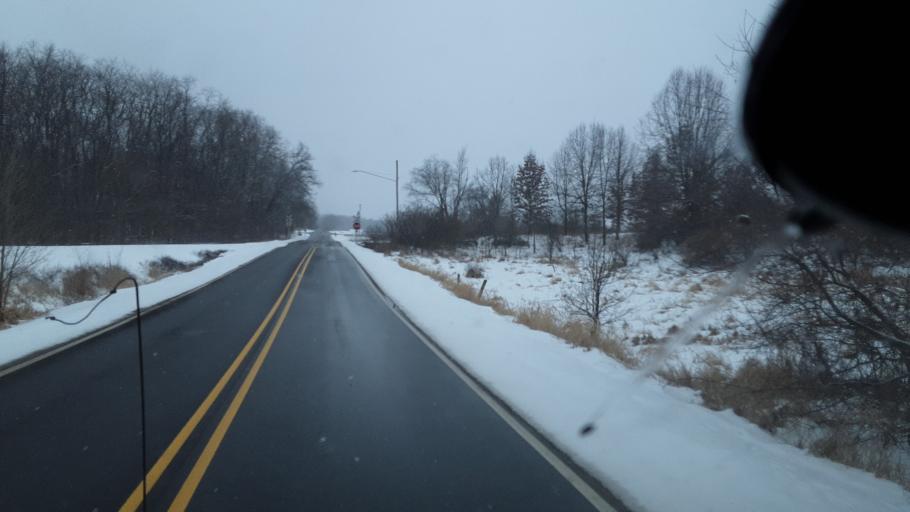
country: US
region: Michigan
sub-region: Ingham County
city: Leslie
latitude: 42.4140
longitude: -84.4433
